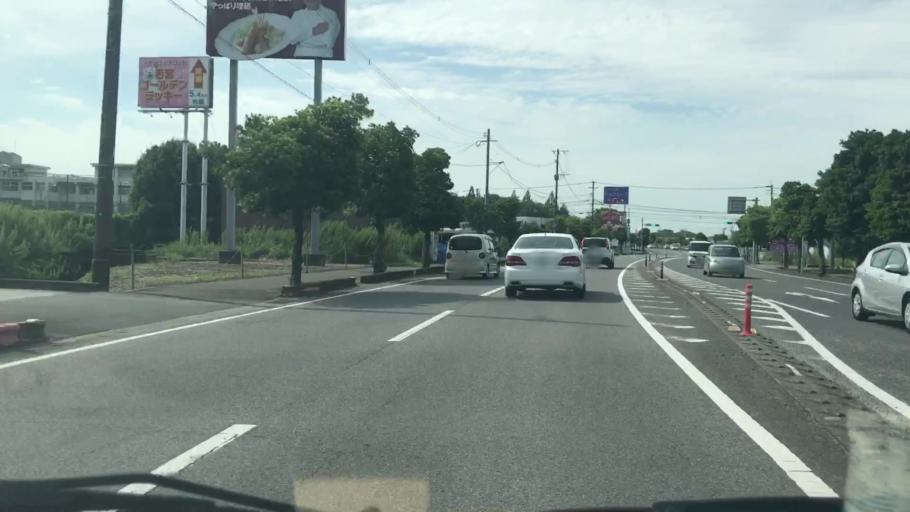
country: JP
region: Saga Prefecture
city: Saga-shi
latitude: 33.3162
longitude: 130.2763
